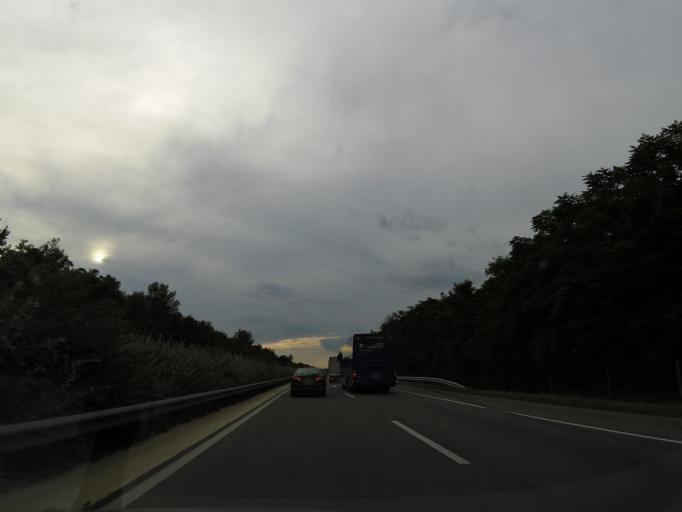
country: HU
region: Pest
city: Inarcs
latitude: 47.2851
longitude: 19.3100
